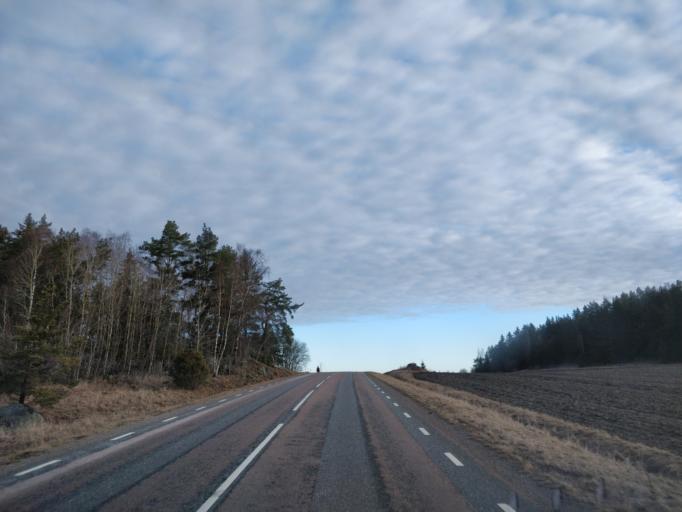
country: SE
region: Uppsala
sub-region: Enkopings Kommun
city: Enkoping
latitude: 59.7608
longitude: 17.0804
